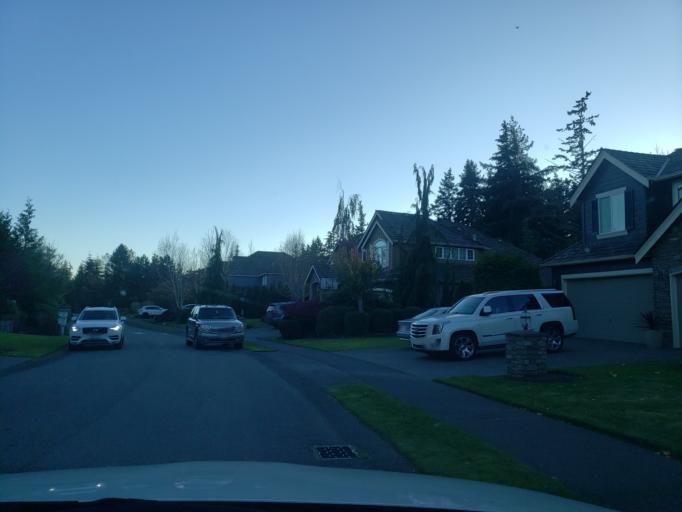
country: US
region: Washington
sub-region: Snohomish County
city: Woodway
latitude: 47.7825
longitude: -122.3795
